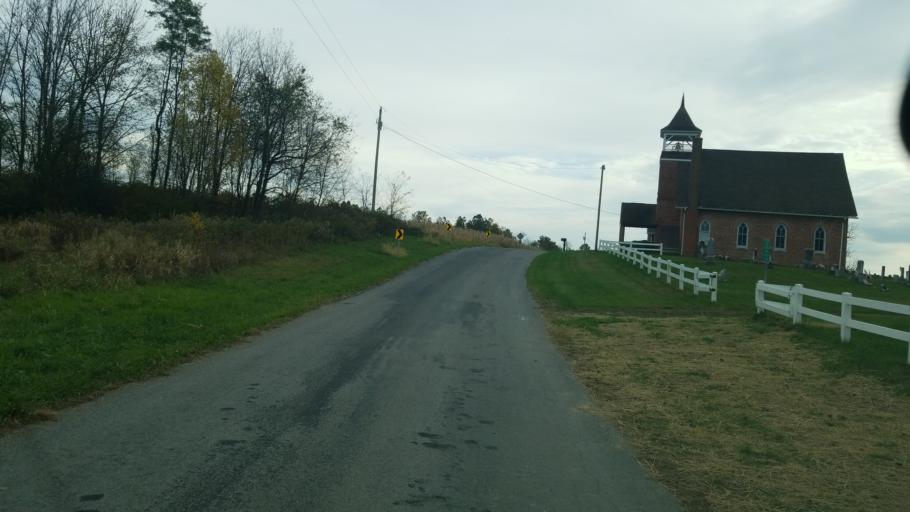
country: US
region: Ohio
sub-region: Ashland County
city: Ashland
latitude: 40.8798
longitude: -82.2265
